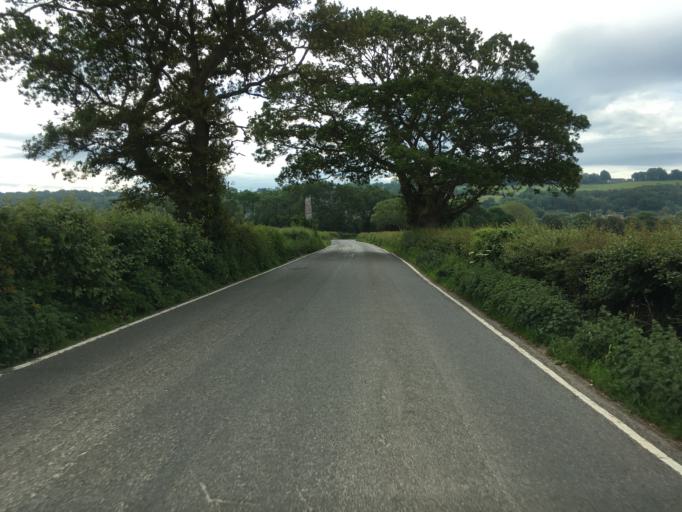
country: GB
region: England
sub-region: North Somerset
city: Portishead
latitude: 51.4689
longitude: -2.7613
